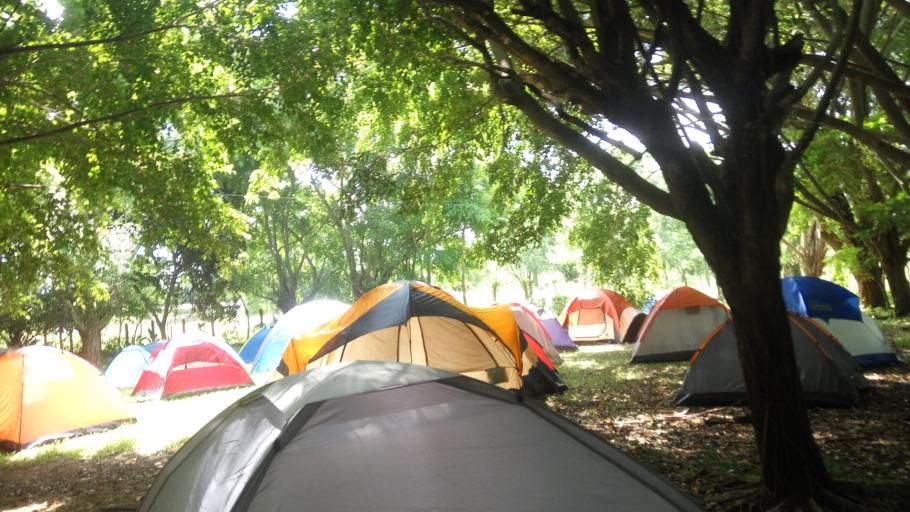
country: MX
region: Tabasco
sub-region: Teapa
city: Eureka y Belen
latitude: 17.5545
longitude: -92.9236
